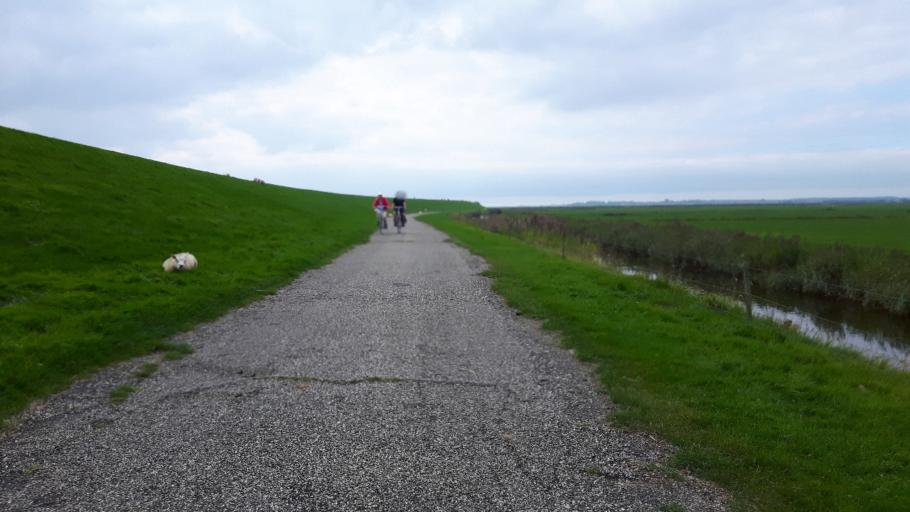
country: NL
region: Friesland
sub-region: Gemeente Ameland
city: Nes
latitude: 53.4443
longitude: 5.8409
